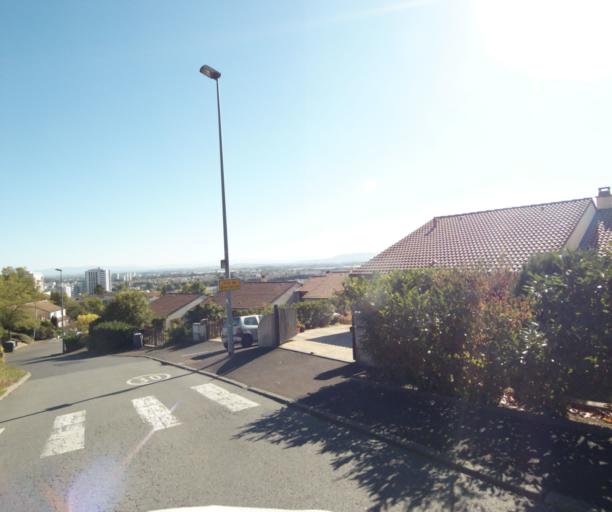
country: FR
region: Auvergne
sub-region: Departement du Puy-de-Dome
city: Cebazat
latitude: 45.8091
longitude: 3.0989
